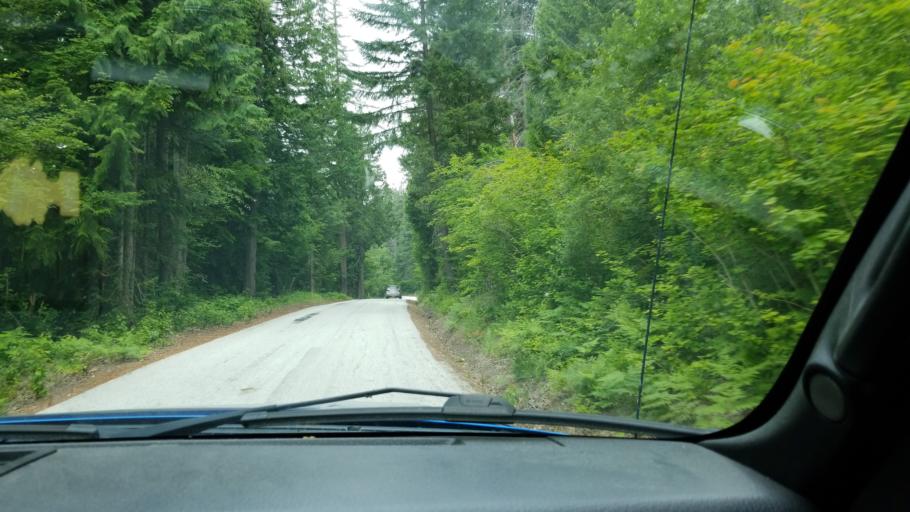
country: US
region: Washington
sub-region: Chelan County
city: Leavenworth
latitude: 47.8571
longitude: -120.8428
